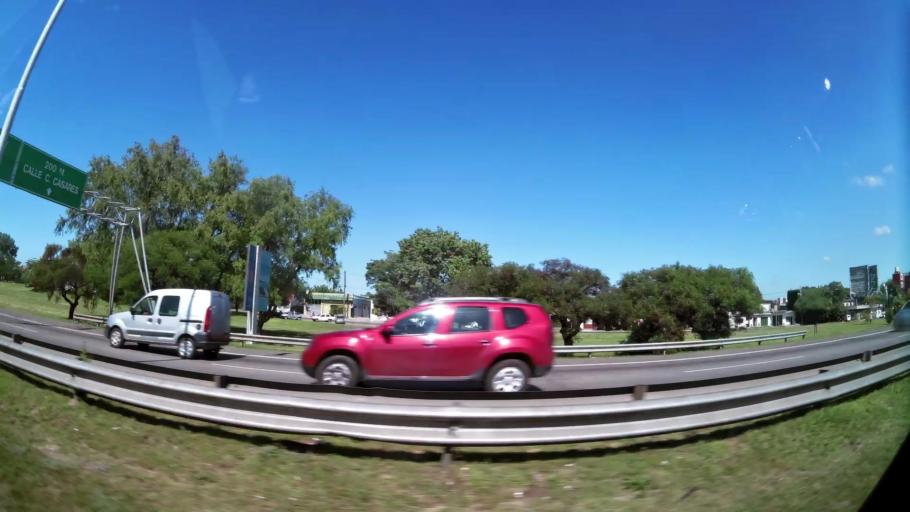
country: AR
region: Buenos Aires
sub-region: Partido de Tigre
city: Tigre
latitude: -34.4628
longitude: -58.5713
